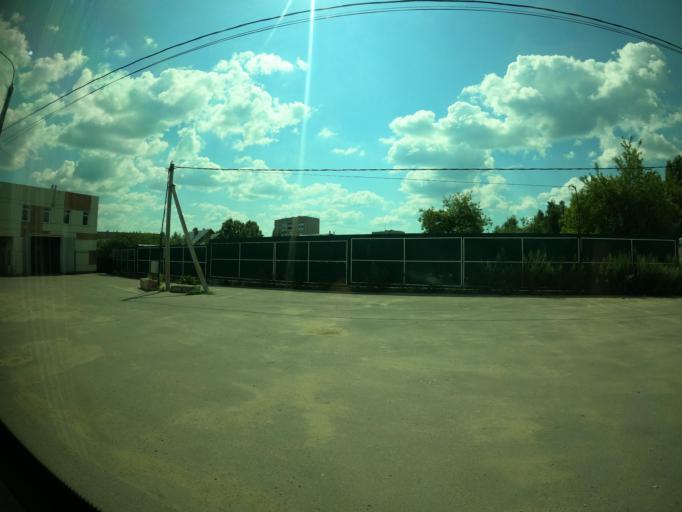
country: RU
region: Moskovskaya
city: Serpukhov
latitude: 54.9051
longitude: 37.3681
